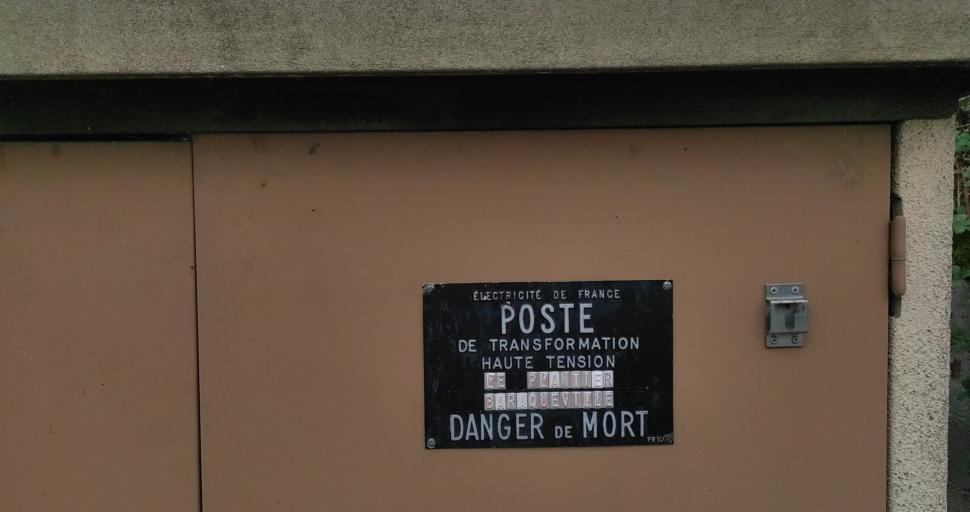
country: FR
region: Midi-Pyrenees
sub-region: Departement de l'Aveyron
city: Baraqueville
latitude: 44.2690
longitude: 2.4347
